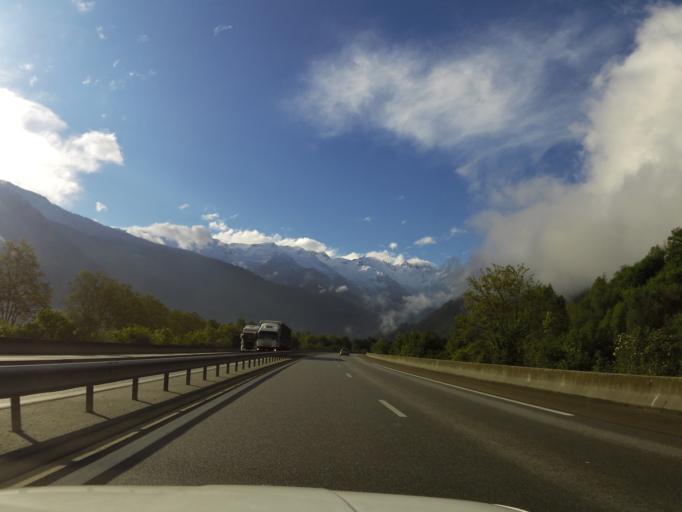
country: FR
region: Rhone-Alpes
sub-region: Departement de la Savoie
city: Aiton
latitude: 45.5546
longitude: 6.2897
